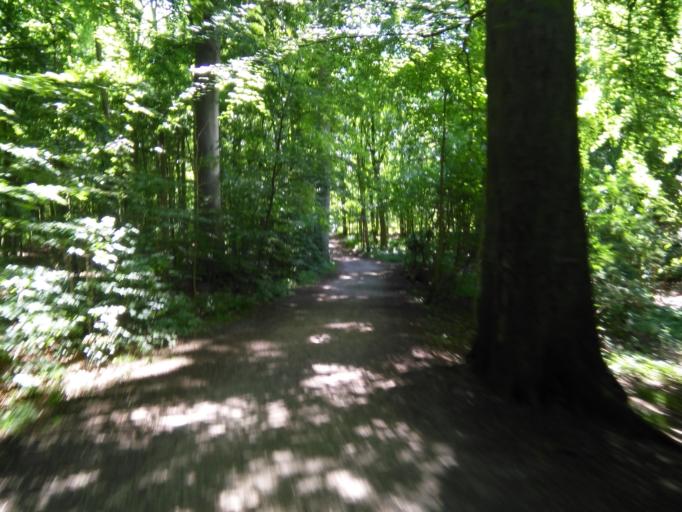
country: DK
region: Central Jutland
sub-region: Arhus Kommune
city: Arhus
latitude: 56.1357
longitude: 10.2060
